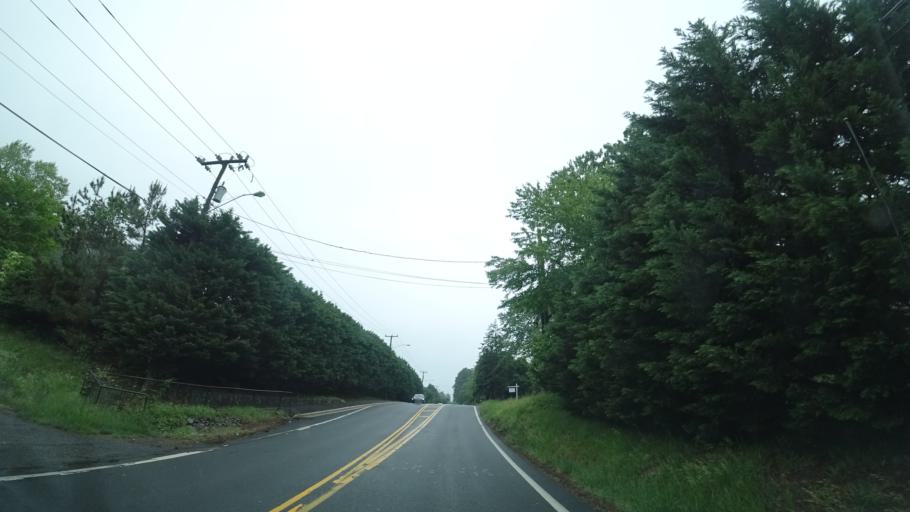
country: US
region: Virginia
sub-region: Fairfax County
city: Tysons Corner
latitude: 38.9380
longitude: -77.2414
